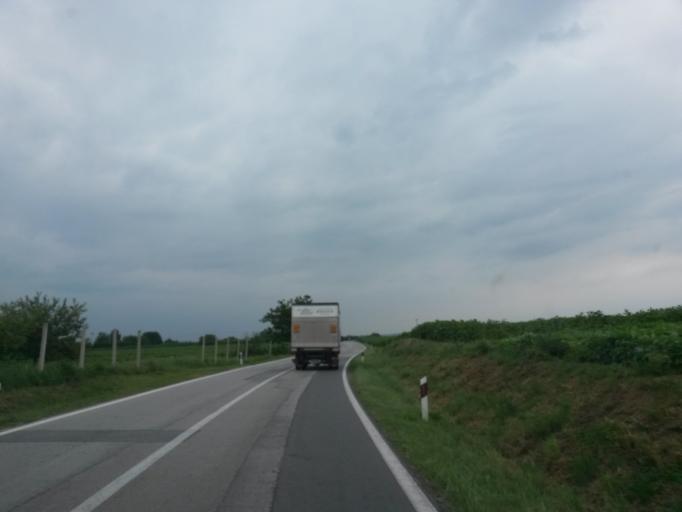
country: HR
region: Vukovarsko-Srijemska
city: Ilok
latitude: 45.2296
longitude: 19.3260
